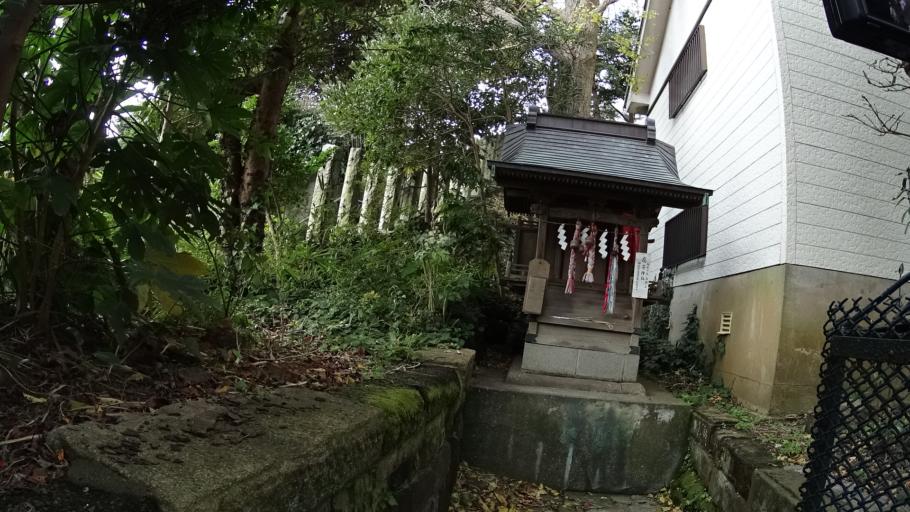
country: JP
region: Kanagawa
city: Miura
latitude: 35.1423
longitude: 139.6188
